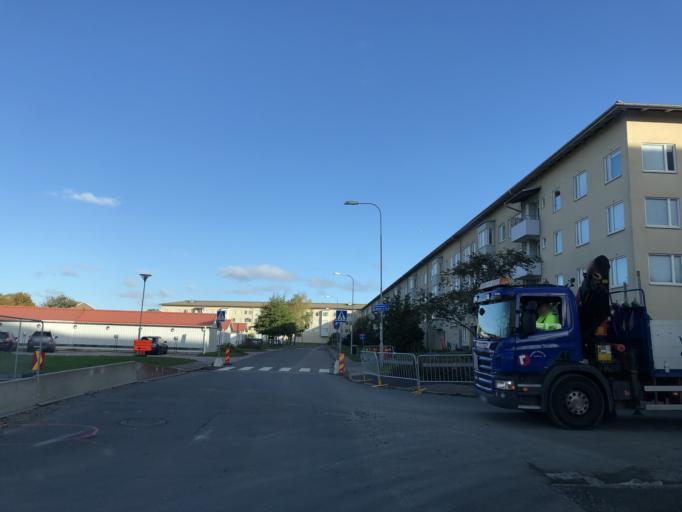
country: SE
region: Vaestra Goetaland
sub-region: Goteborg
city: Majorna
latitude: 57.6551
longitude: 11.9032
